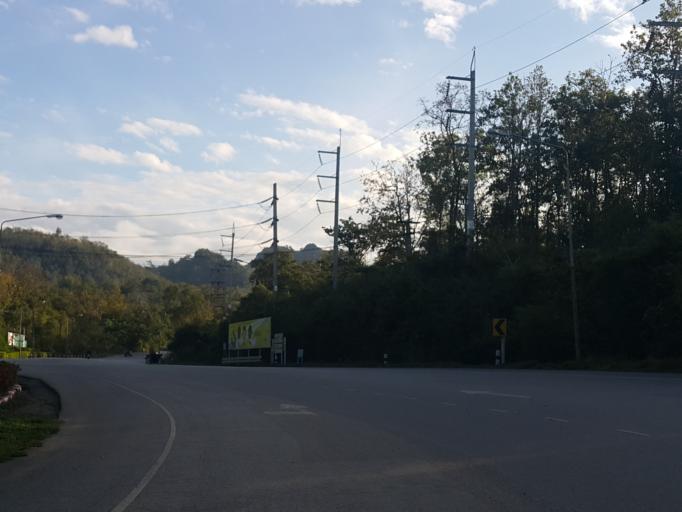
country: TH
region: Lampang
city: Chae Hom
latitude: 18.5434
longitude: 99.5669
